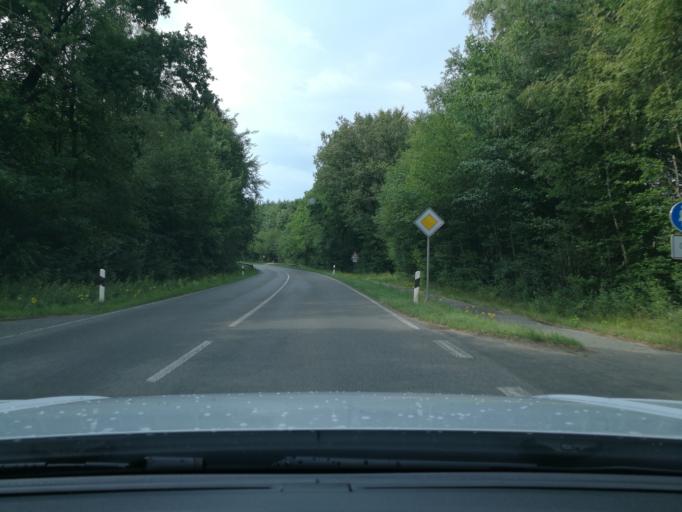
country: DE
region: Schleswig-Holstein
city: Dassendorf
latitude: 53.5073
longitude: 10.3656
